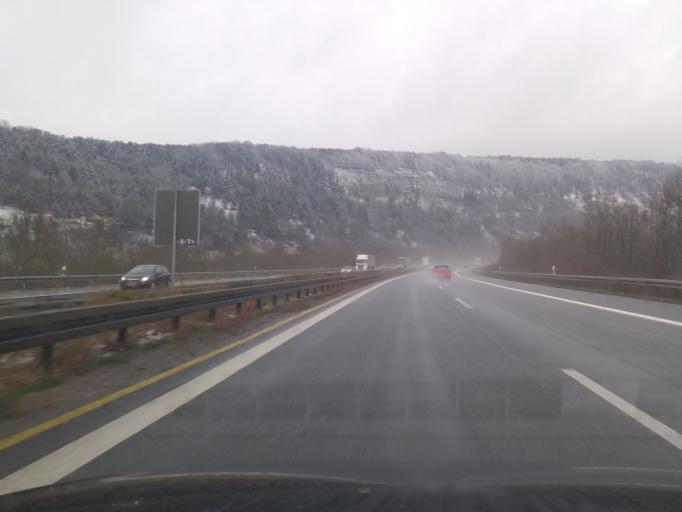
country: DE
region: Bavaria
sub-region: Regierungsbezirk Unterfranken
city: Elfershausen
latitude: 50.1382
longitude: 9.9510
